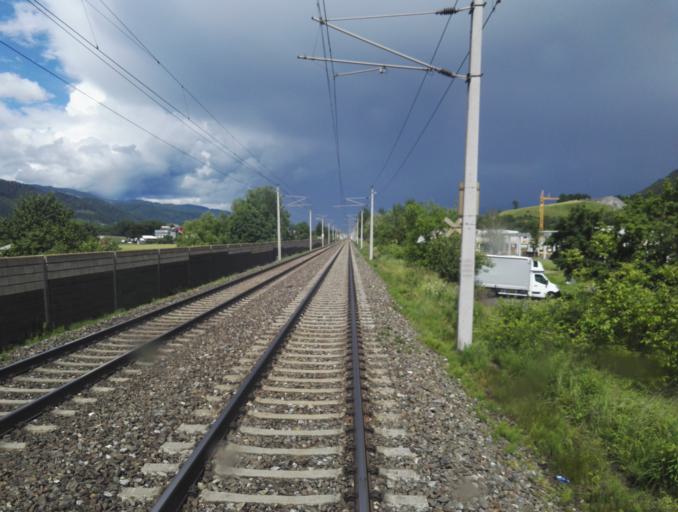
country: AT
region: Styria
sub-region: Politischer Bezirk Bruck-Muerzzuschlag
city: Sankt Marein im Muerztal
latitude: 47.4588
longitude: 15.3391
